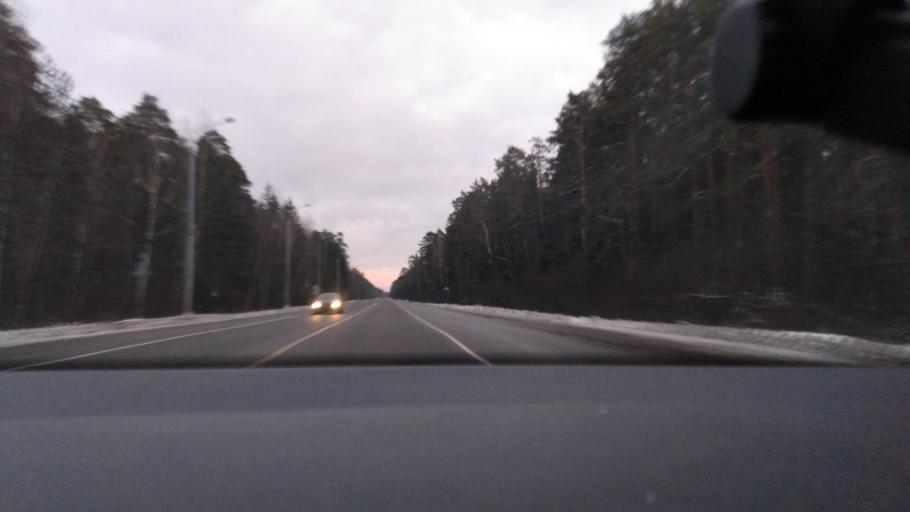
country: RU
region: Moskovskaya
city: Il'inskiy Pogost
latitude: 55.4582
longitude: 38.9884
